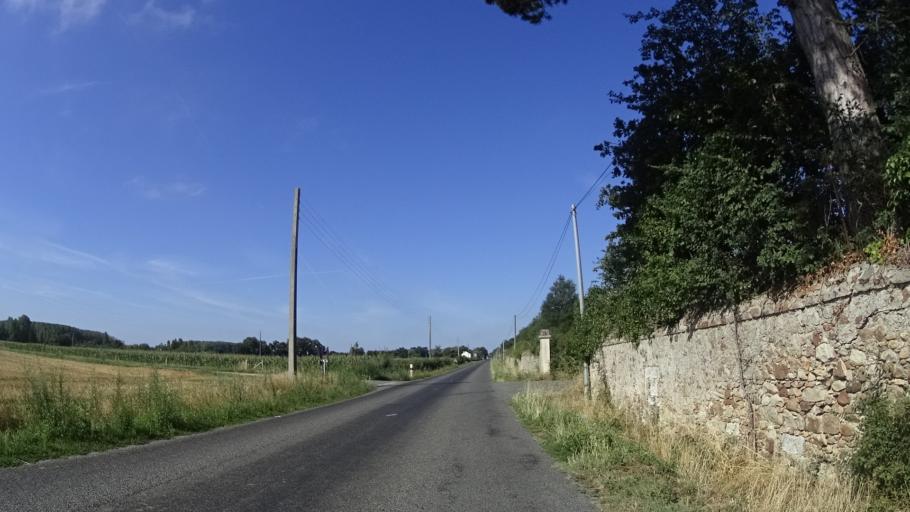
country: FR
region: Pays de la Loire
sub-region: Departement de Maine-et-Loire
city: Etriche
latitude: 47.6285
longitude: -0.4457
